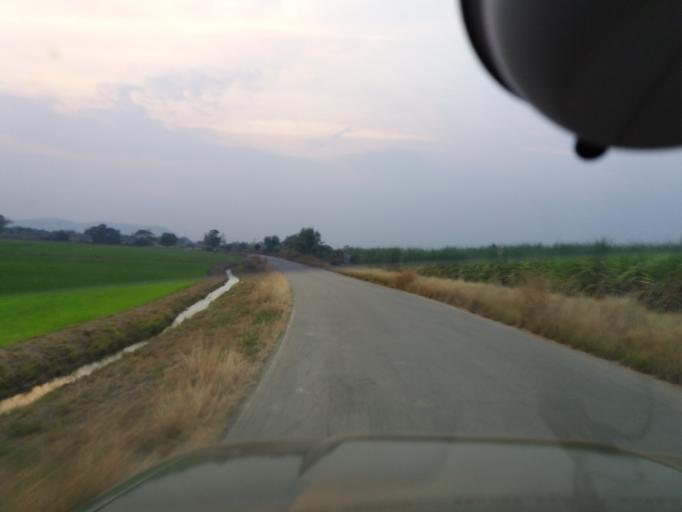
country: TH
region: Suphan Buri
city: Doem Bang Nang Buat
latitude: 14.8879
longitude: 100.1342
